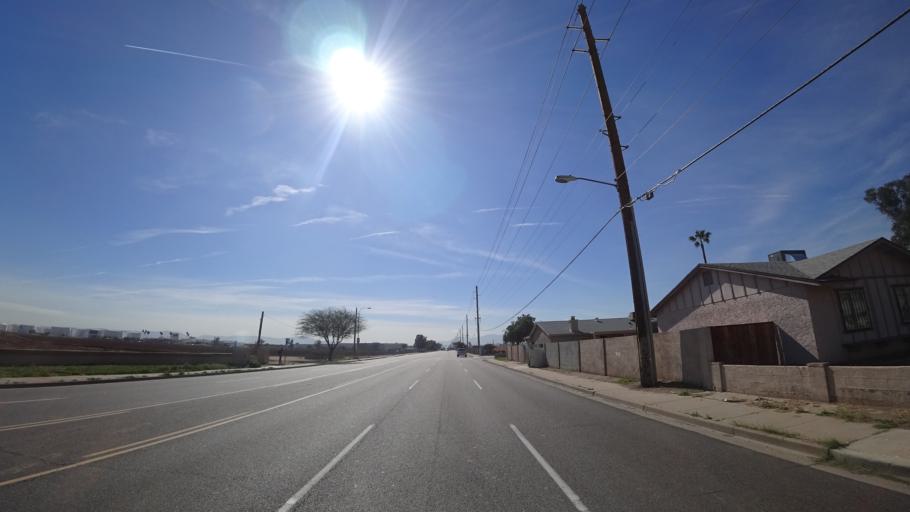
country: US
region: Arizona
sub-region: Maricopa County
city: Tolleson
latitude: 33.4559
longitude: -112.1866
